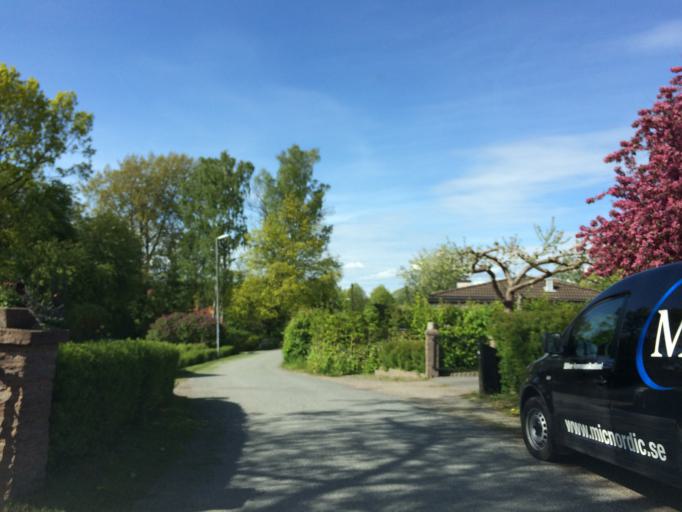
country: SE
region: Stockholm
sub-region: Sollentuna Kommun
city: Sollentuna
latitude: 59.4583
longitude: 17.9178
